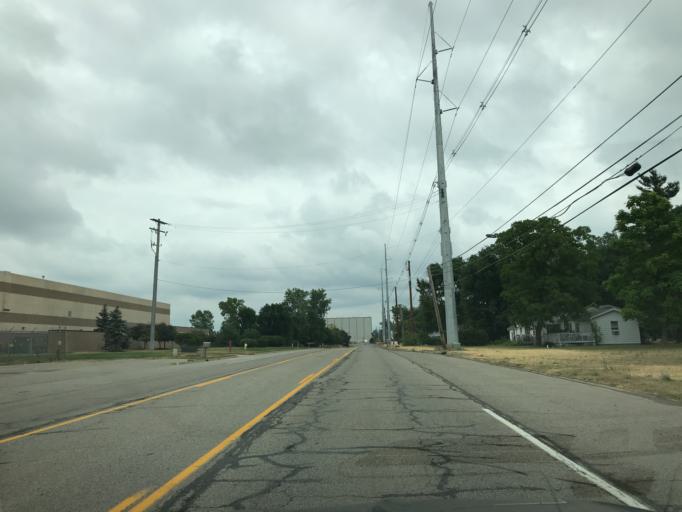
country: US
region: Michigan
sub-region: Eaton County
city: Waverly
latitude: 42.6975
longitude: -84.6483
